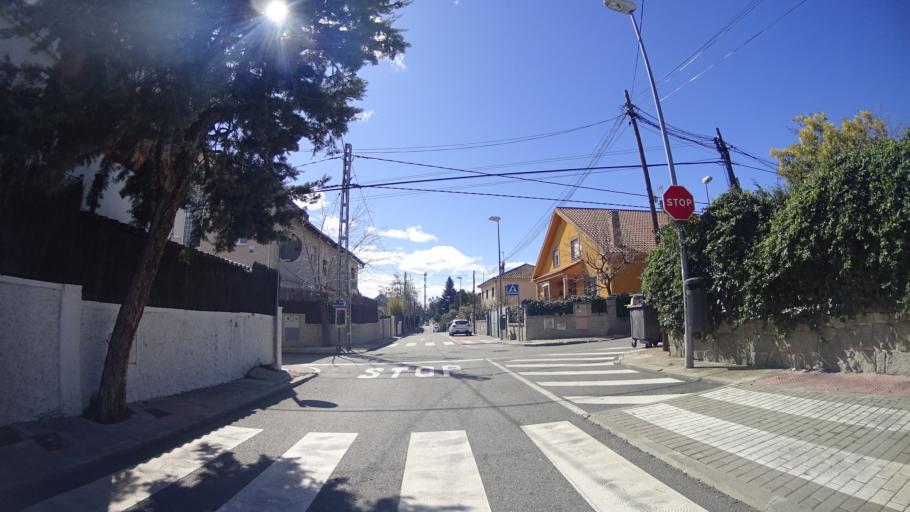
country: ES
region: Madrid
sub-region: Provincia de Madrid
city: Las Matas
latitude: 40.5553
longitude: -3.8965
